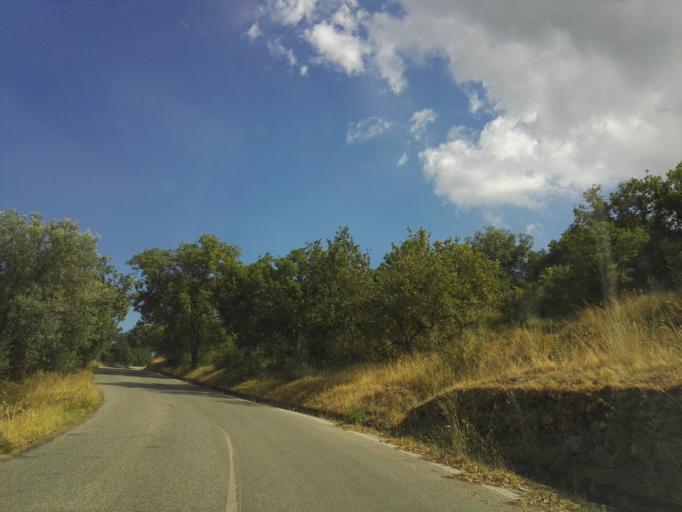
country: IT
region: Calabria
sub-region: Provincia di Reggio Calabria
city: Camini
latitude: 38.4255
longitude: 16.4872
